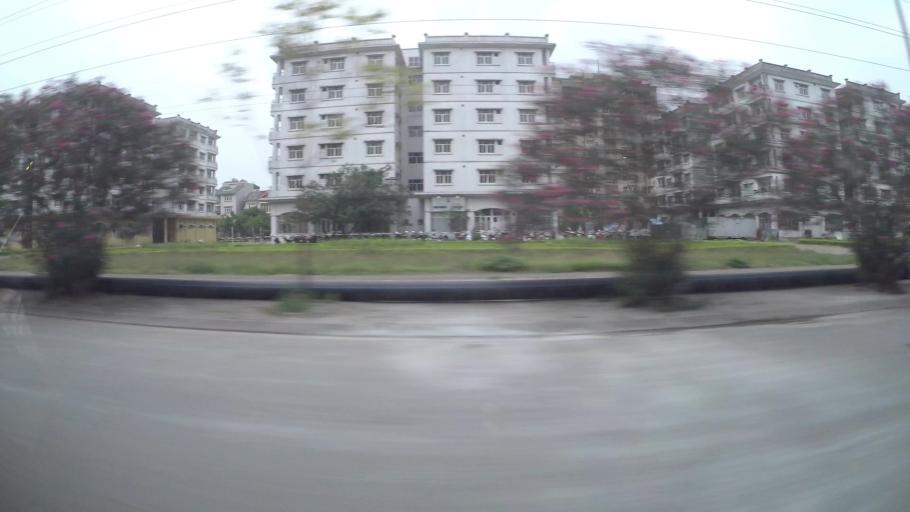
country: VN
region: Ha Noi
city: Trau Quy
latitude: 21.0383
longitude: 105.9072
